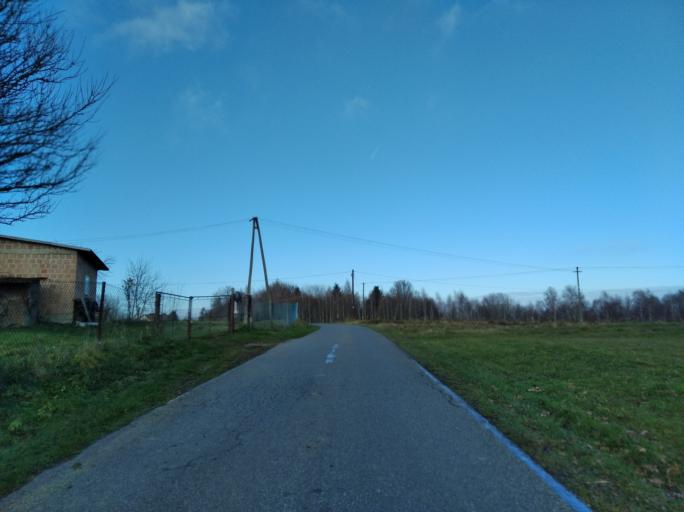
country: PL
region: Subcarpathian Voivodeship
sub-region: Powiat strzyzowski
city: Czudec
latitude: 49.9137
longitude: 21.8463
